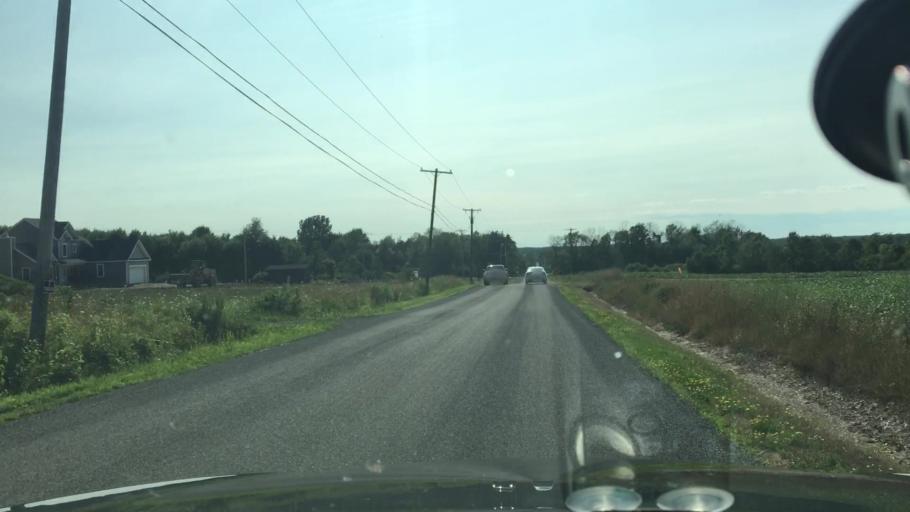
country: US
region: New York
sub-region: Erie County
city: North Collins
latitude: 42.6198
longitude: -78.9221
